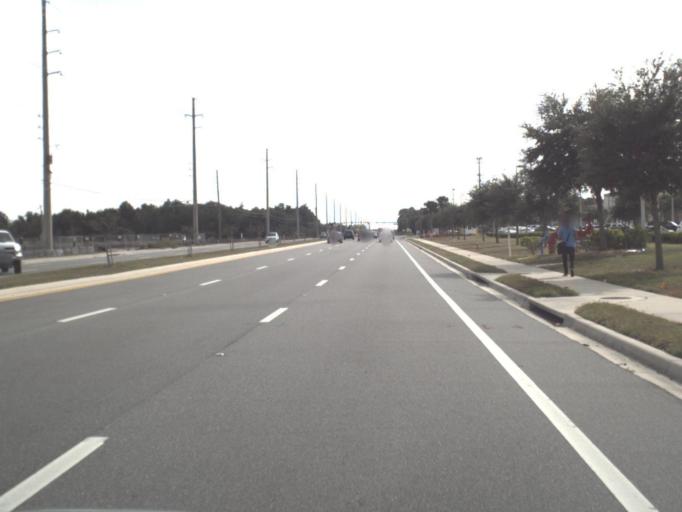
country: US
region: Florida
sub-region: Osceola County
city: Buenaventura Lakes
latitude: 28.3825
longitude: -81.2446
